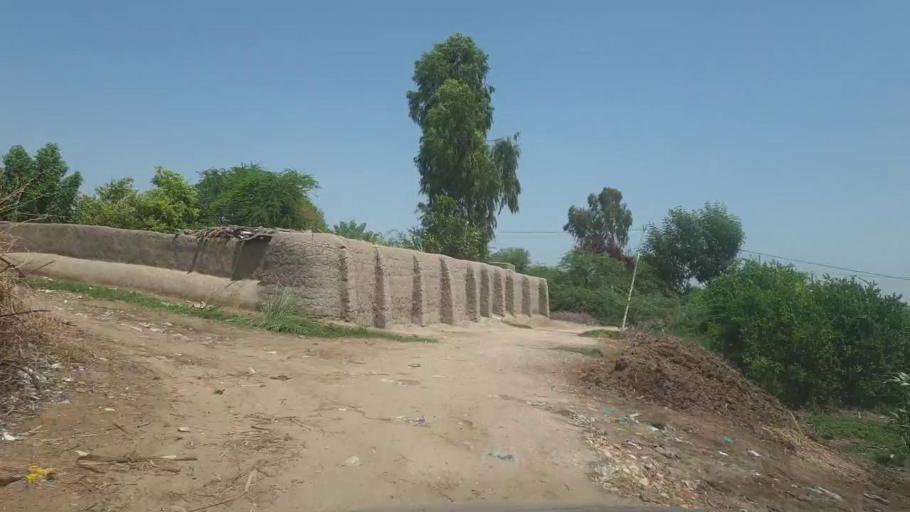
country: PK
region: Sindh
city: Kot Diji
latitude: 27.3331
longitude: 69.0095
